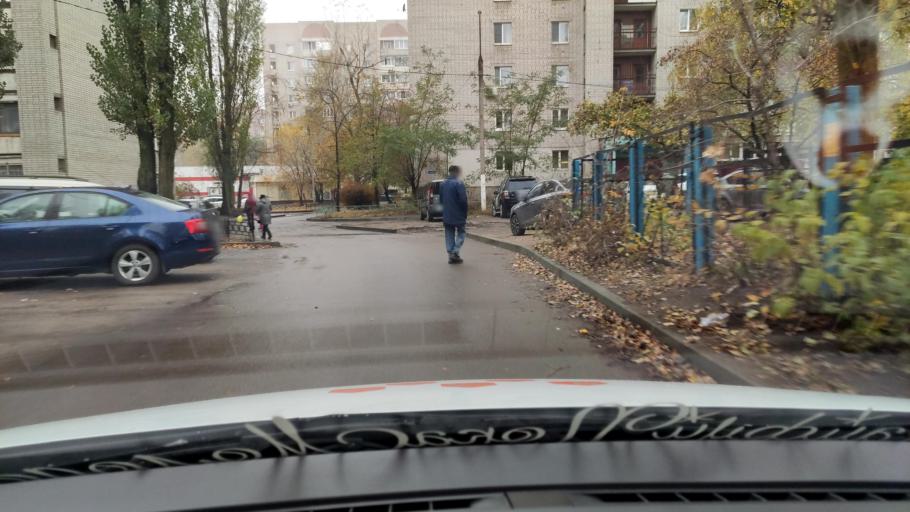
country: RU
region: Voronezj
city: Podgornoye
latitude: 51.6987
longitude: 39.1442
